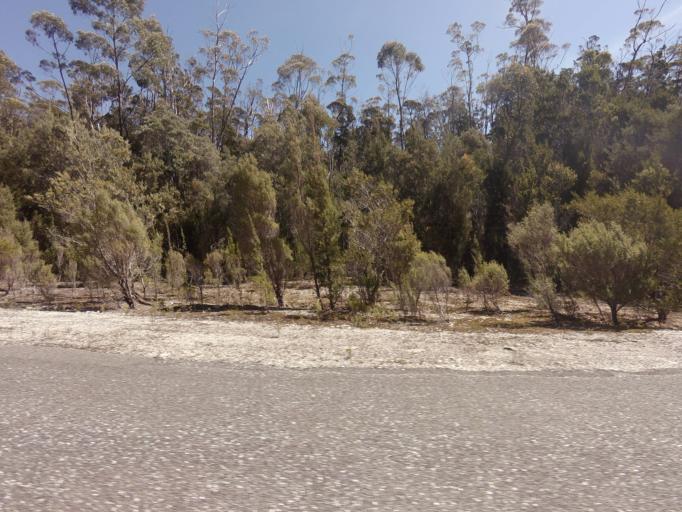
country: AU
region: Tasmania
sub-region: West Coast
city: Queenstown
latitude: -42.7620
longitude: 146.0049
